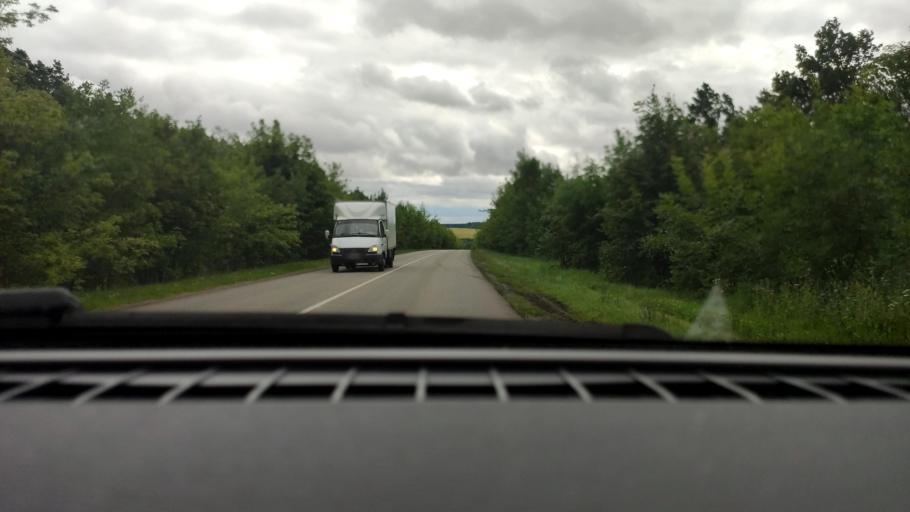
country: RU
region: Voronezj
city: Zemlyansk
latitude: 51.8866
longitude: 38.7573
